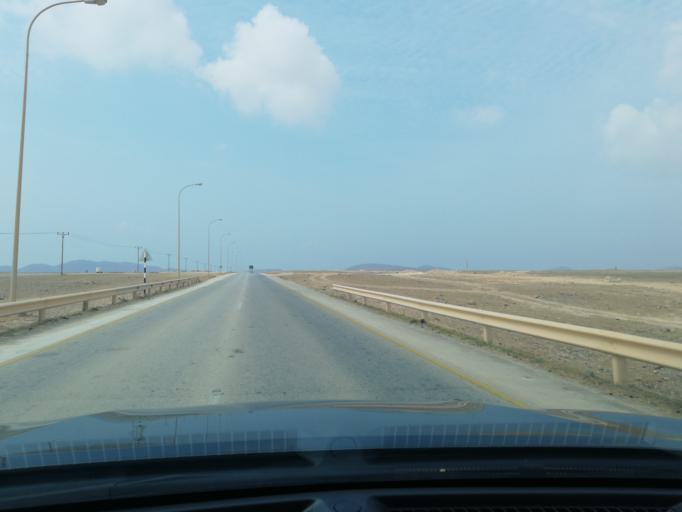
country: OM
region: Zufar
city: Salalah
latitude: 16.9357
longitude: 53.8436
